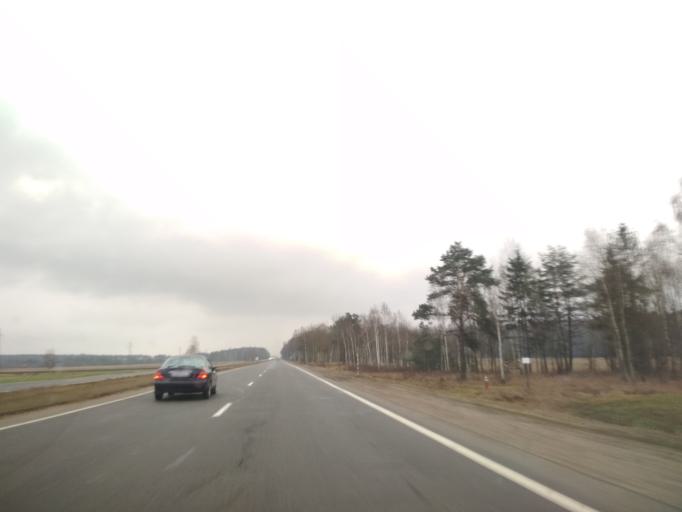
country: BY
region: Minsk
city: Dukora
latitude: 53.6303
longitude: 28.0228
